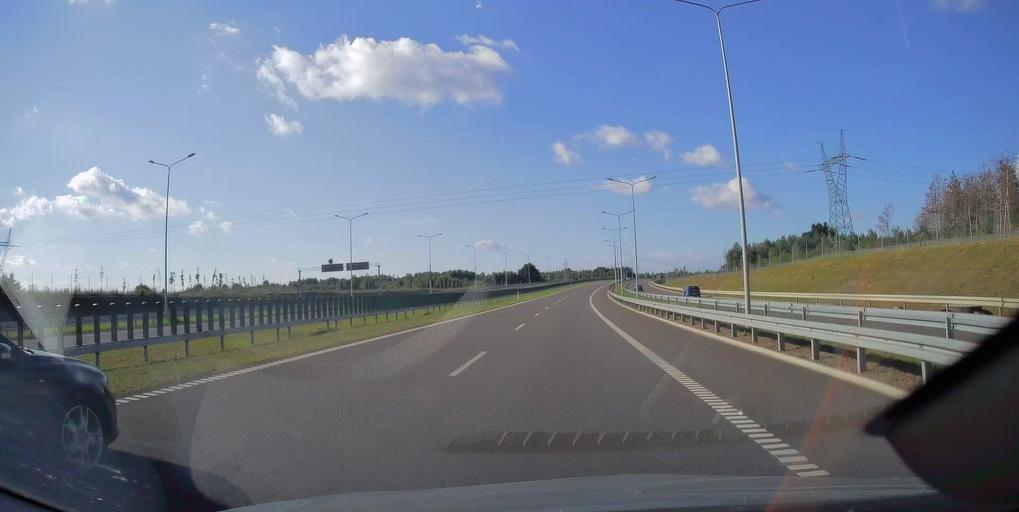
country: PL
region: Masovian Voivodeship
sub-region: Powiat szydlowiecki
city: Oronsko
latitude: 51.3332
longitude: 21.0150
